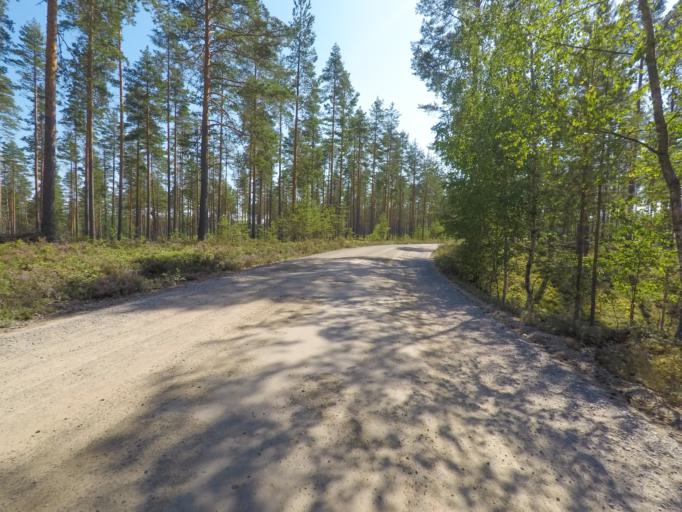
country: FI
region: Southern Savonia
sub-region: Mikkeli
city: Puumala
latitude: 61.4201
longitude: 28.0426
